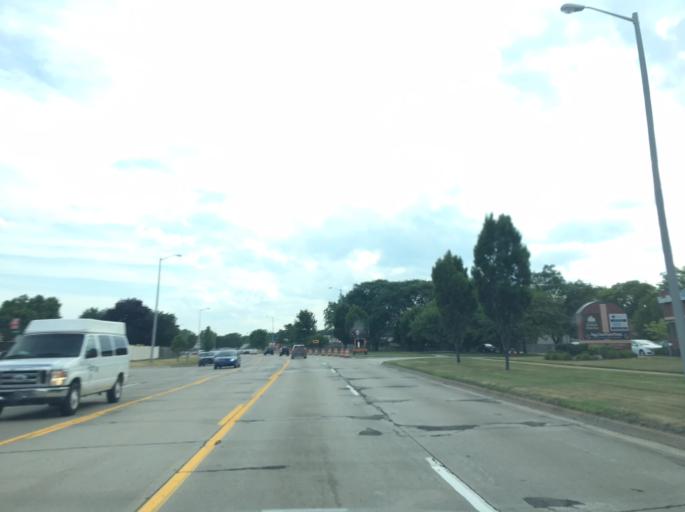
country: US
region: Michigan
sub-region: Macomb County
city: Fraser
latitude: 42.5554
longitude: -82.9889
